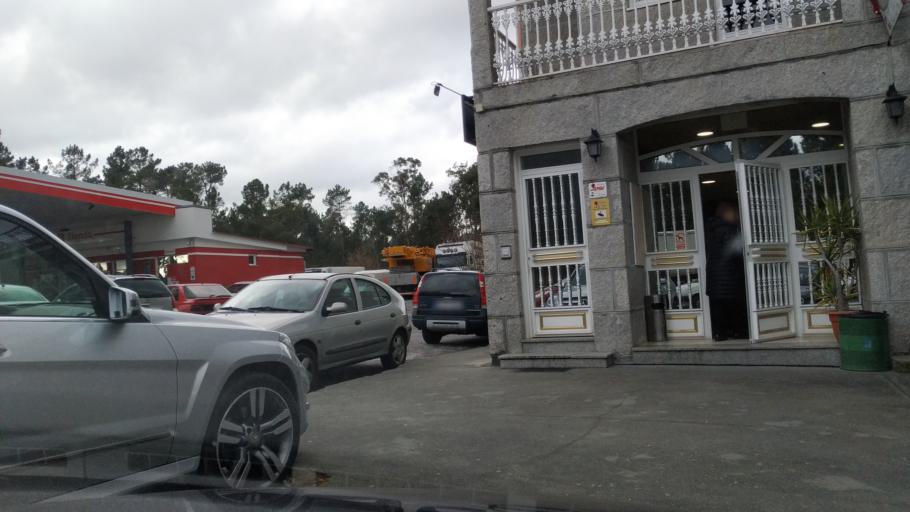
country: ES
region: Galicia
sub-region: Provincia de Ourense
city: Maside
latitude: 42.4534
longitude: -8.0262
